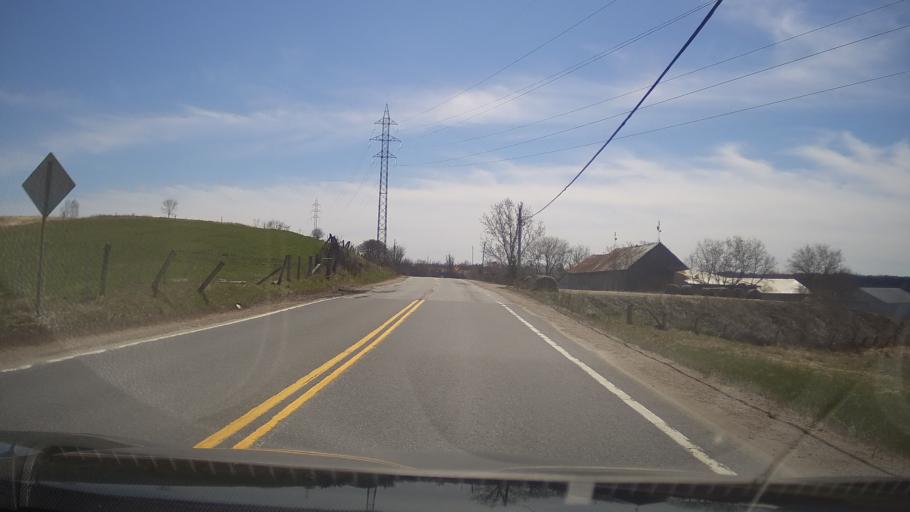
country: CA
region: Quebec
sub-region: Outaouais
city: Wakefield
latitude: 45.4967
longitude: -75.9578
